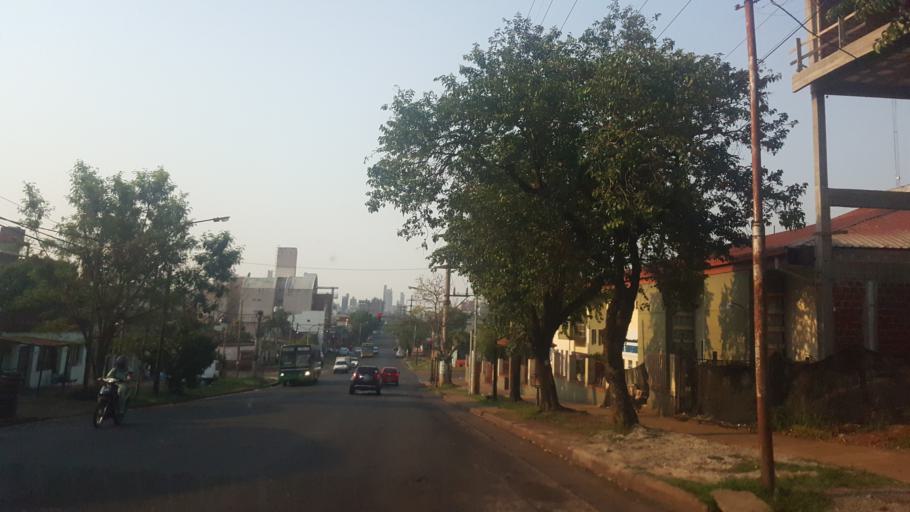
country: AR
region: Misiones
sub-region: Departamento de Capital
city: Posadas
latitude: -27.3826
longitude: -55.8921
